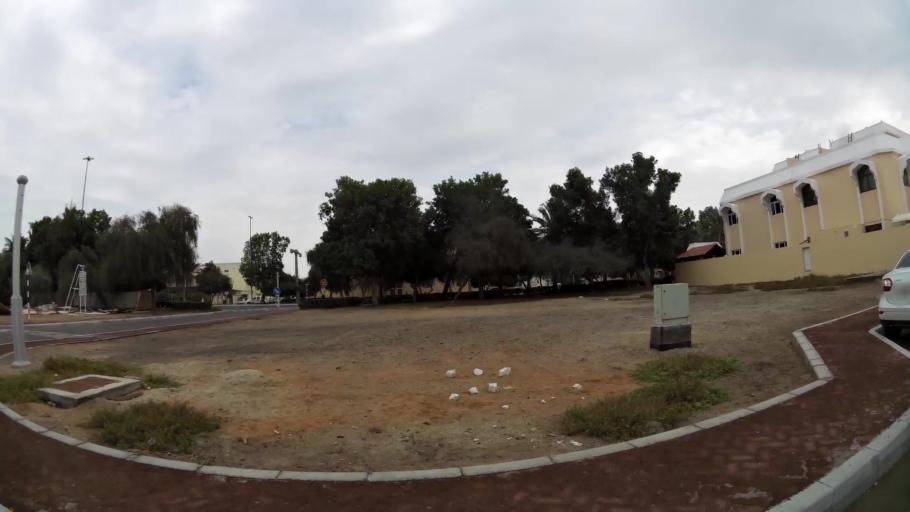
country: AE
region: Abu Dhabi
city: Abu Dhabi
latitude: 24.4314
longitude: 54.4124
